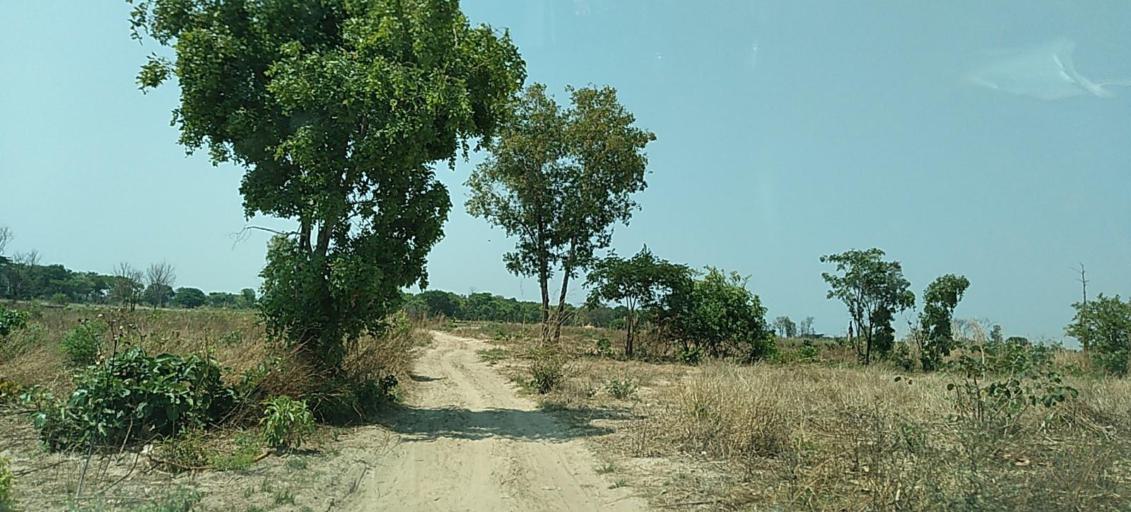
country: ZM
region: Copperbelt
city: Mpongwe
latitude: -13.8610
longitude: 28.0551
